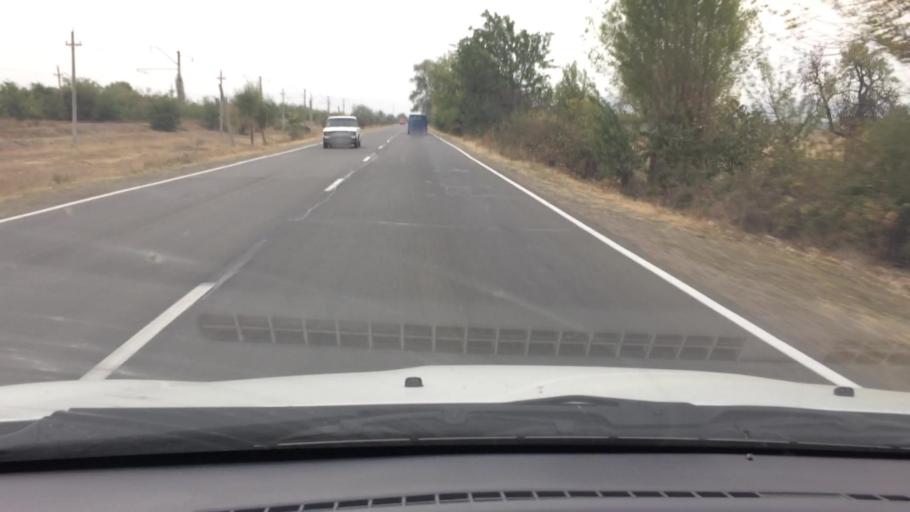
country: GE
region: Kvemo Kartli
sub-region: Marneuli
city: Marneuli
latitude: 41.4454
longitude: 44.8156
